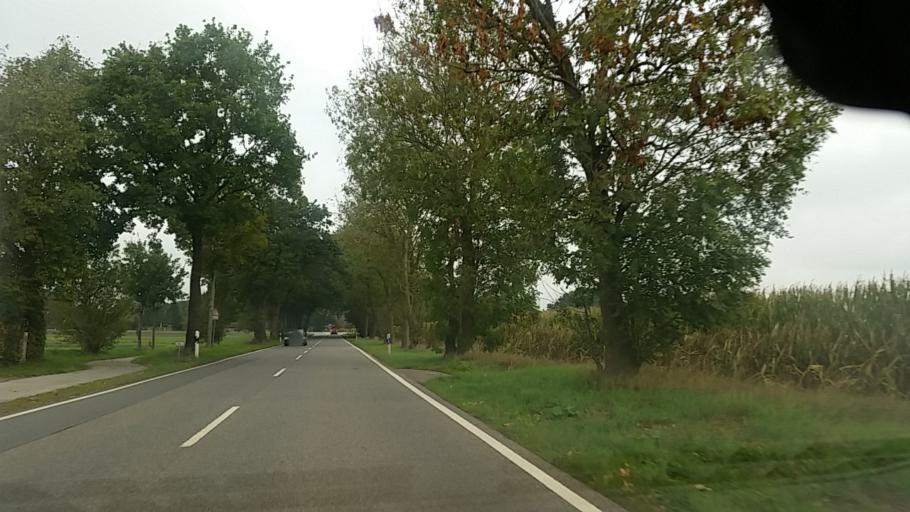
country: DE
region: Schleswig-Holstein
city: Hasenmoor
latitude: 53.8974
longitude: 9.9788
